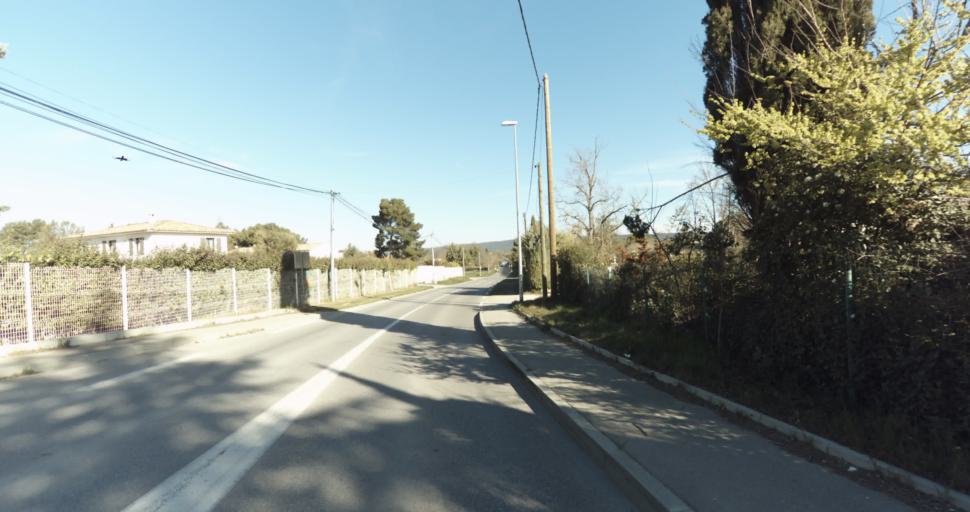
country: FR
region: Provence-Alpes-Cote d'Azur
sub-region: Departement des Bouches-du-Rhone
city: Aix-en-Provence
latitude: 43.5689
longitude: 5.4254
